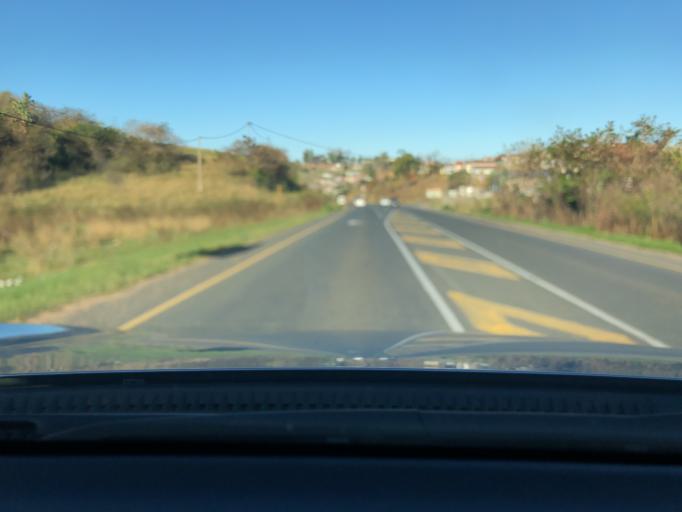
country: ZA
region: KwaZulu-Natal
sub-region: eThekwini Metropolitan Municipality
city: Umkomaas
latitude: -30.0352
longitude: 30.8137
